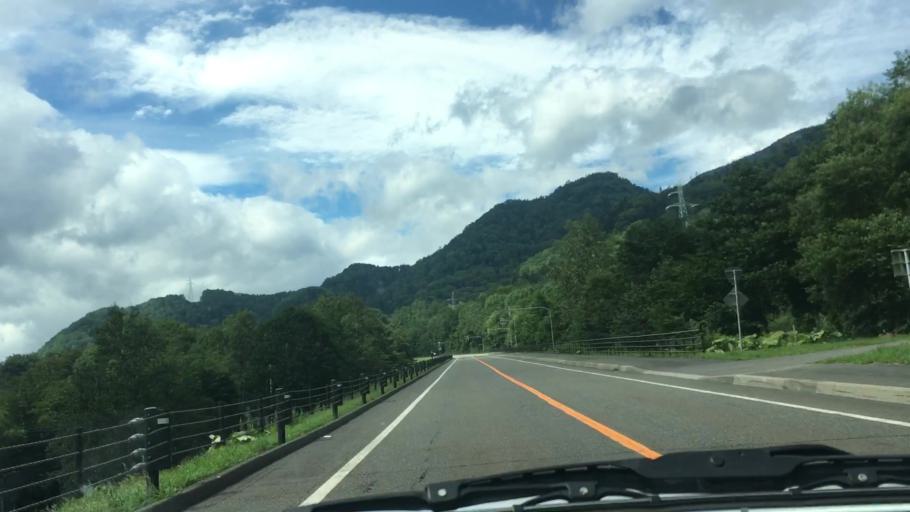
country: JP
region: Hokkaido
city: Otofuke
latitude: 43.3633
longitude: 143.2355
